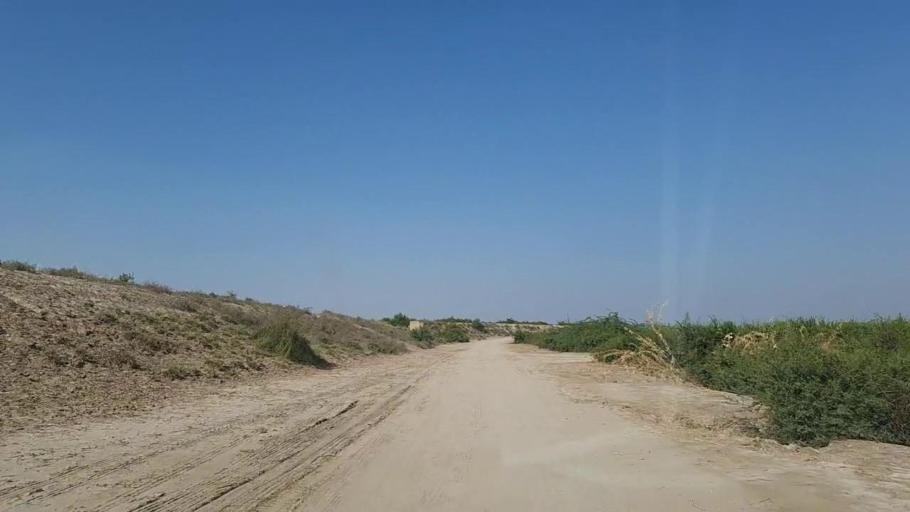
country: PK
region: Sindh
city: Chuhar Jamali
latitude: 24.5780
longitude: 68.0296
